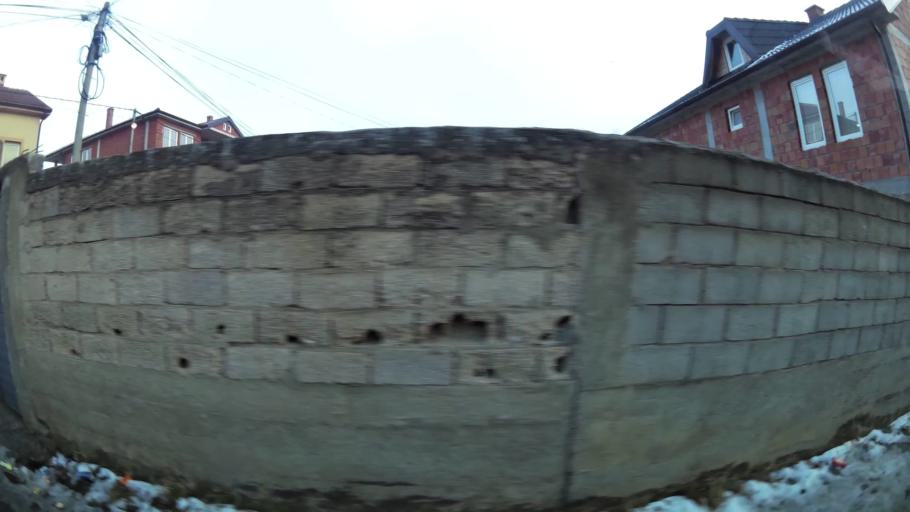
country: MK
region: Aracinovo
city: Arachinovo
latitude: 42.0264
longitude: 21.5629
